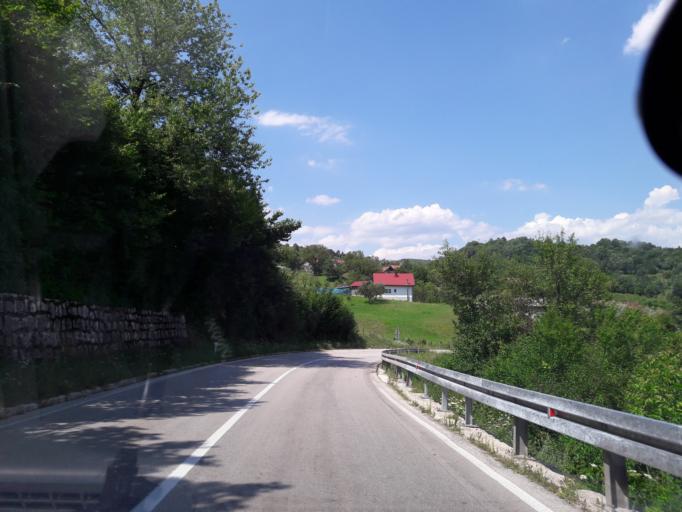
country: BA
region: Republika Srpska
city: Mrkonjic Grad
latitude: 44.4190
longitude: 17.1065
